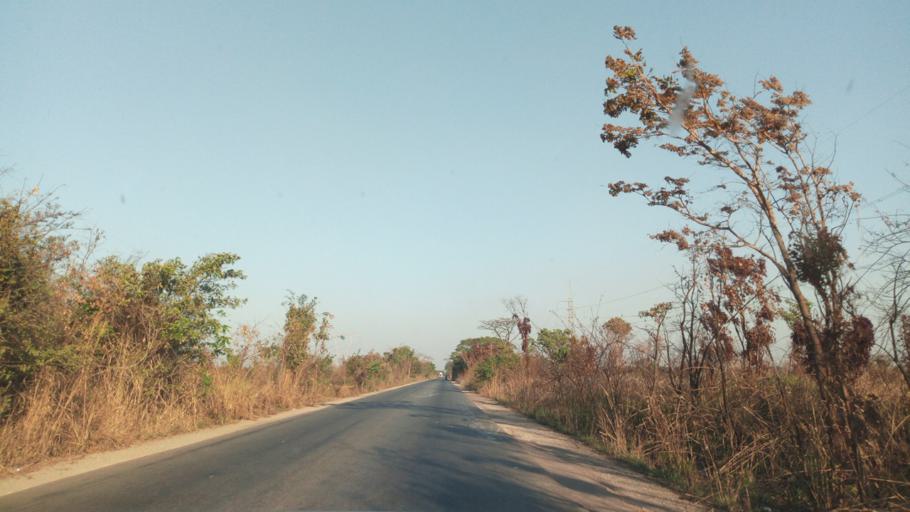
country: CD
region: Katanga
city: Likasi
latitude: -11.1172
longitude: 27.0287
